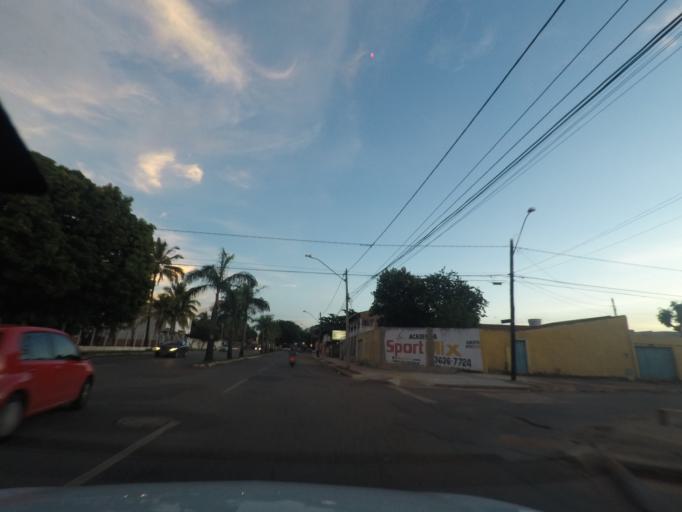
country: BR
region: Goias
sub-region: Goiania
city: Goiania
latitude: -16.6984
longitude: -49.3116
